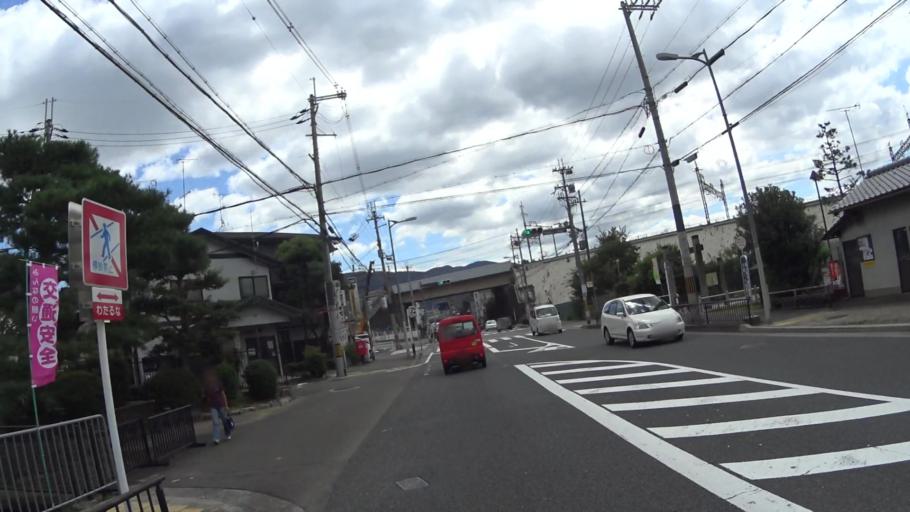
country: JP
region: Kyoto
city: Kyoto
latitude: 34.9934
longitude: 135.8060
